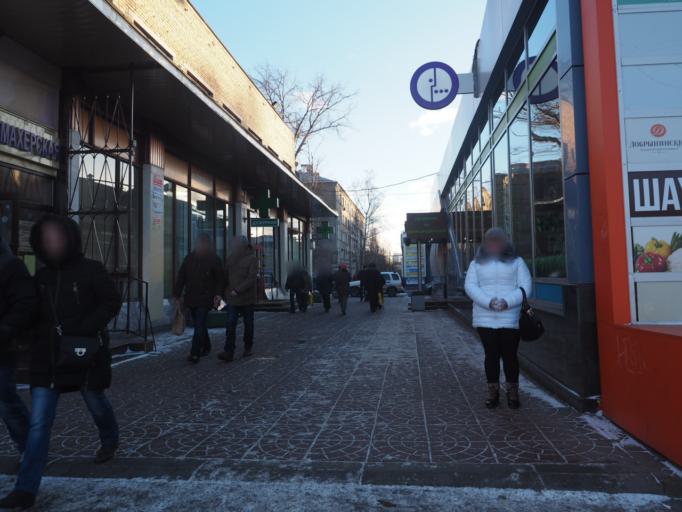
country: RU
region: Moscow
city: Metrogorodok
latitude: 55.8079
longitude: 37.7990
